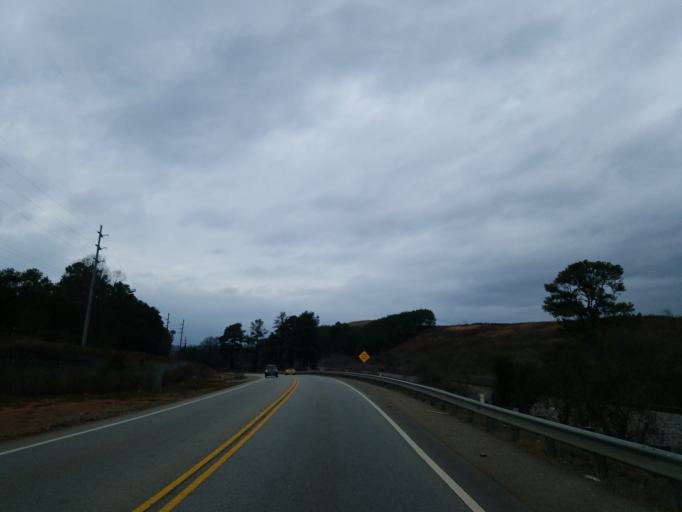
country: US
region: Georgia
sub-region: Bartow County
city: Emerson
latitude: 34.1352
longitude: -84.7603
